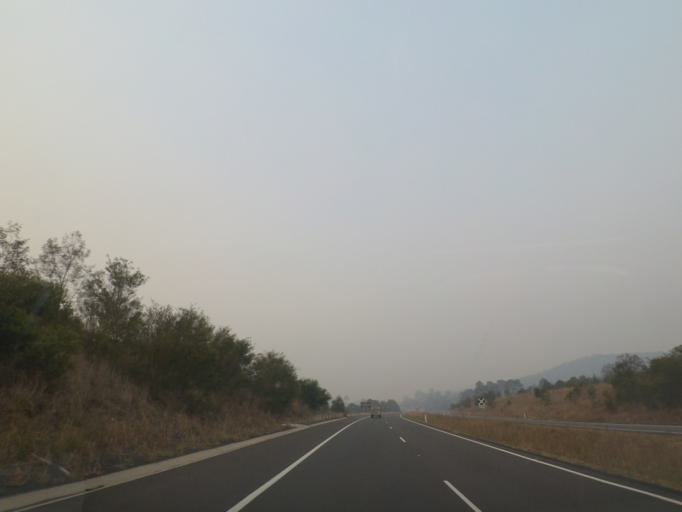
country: AU
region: New South Wales
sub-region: Nambucca Shire
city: Macksville
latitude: -30.7561
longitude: 152.9066
